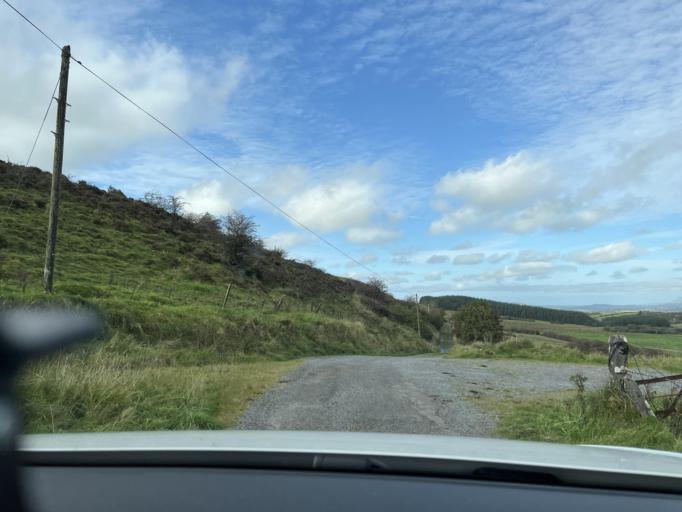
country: IE
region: Connaught
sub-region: Sligo
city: Ballymote
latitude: 54.0605
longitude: -8.4228
